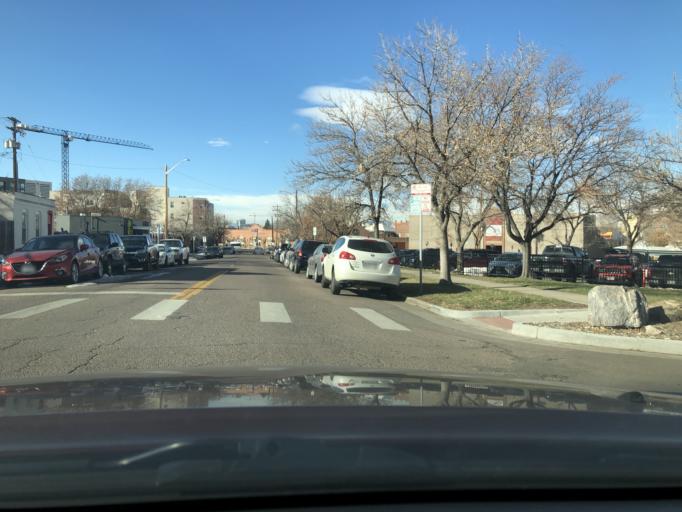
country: US
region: Colorado
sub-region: Denver County
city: Denver
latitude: 39.7547
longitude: -104.9757
